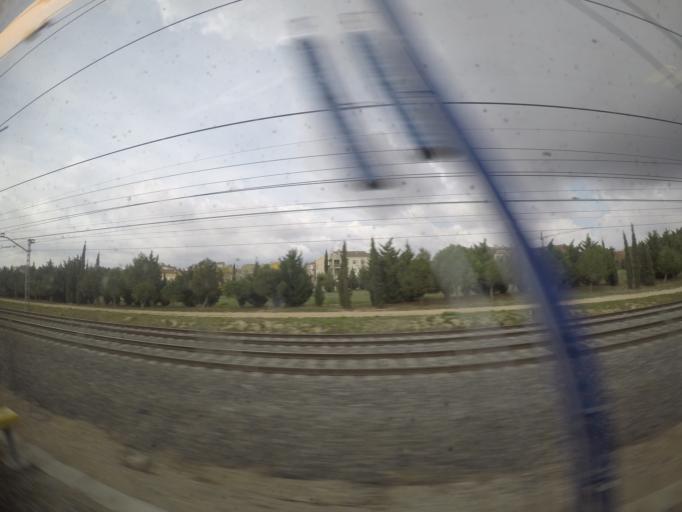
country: ES
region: Catalonia
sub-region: Provincia de Barcelona
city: Castellet
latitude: 41.2880
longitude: 1.6170
